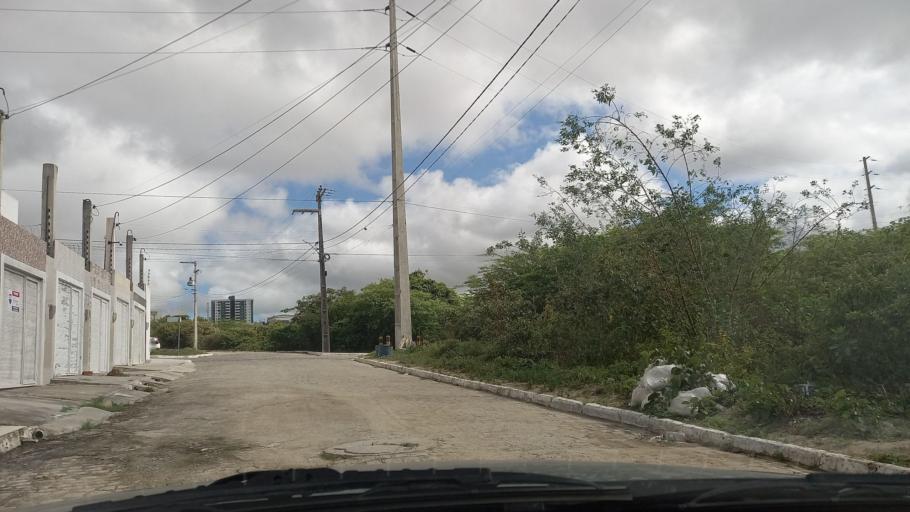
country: BR
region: Pernambuco
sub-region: Caruaru
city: Caruaru
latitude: -8.3070
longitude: -35.9558
